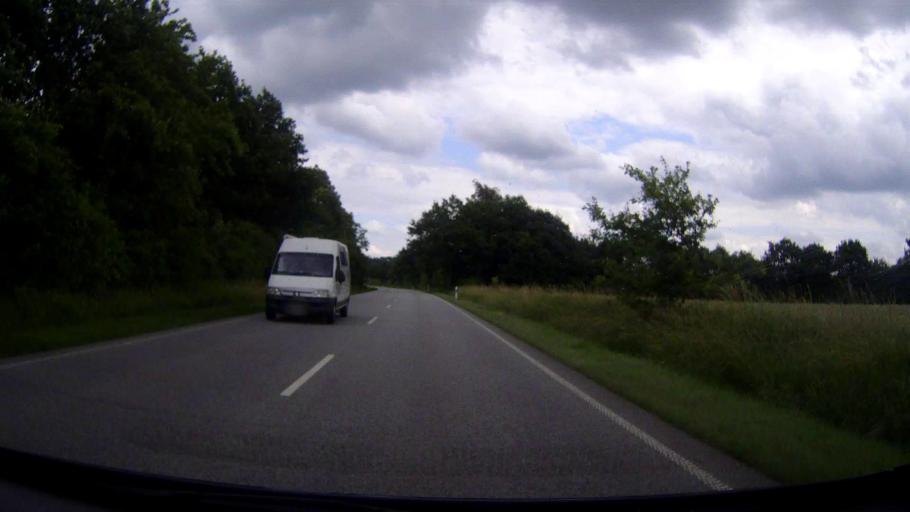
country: DE
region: Schleswig-Holstein
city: Jahrsdorf
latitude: 54.0755
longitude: 9.6241
